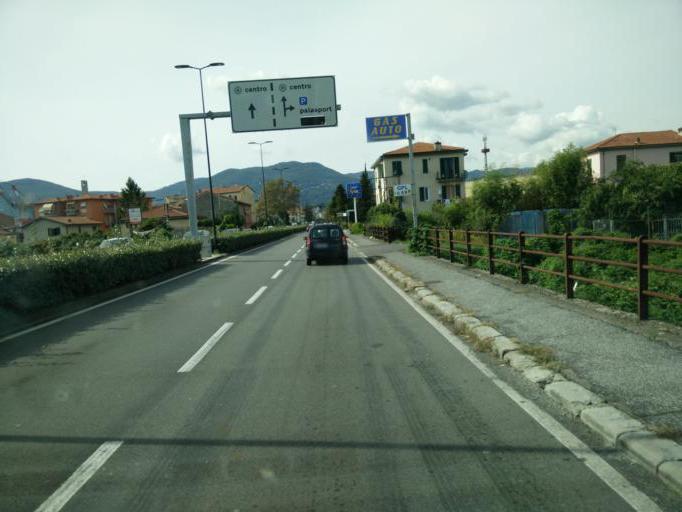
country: IT
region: Liguria
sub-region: Provincia di La Spezia
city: La Spezia
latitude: 44.1138
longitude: 9.8508
